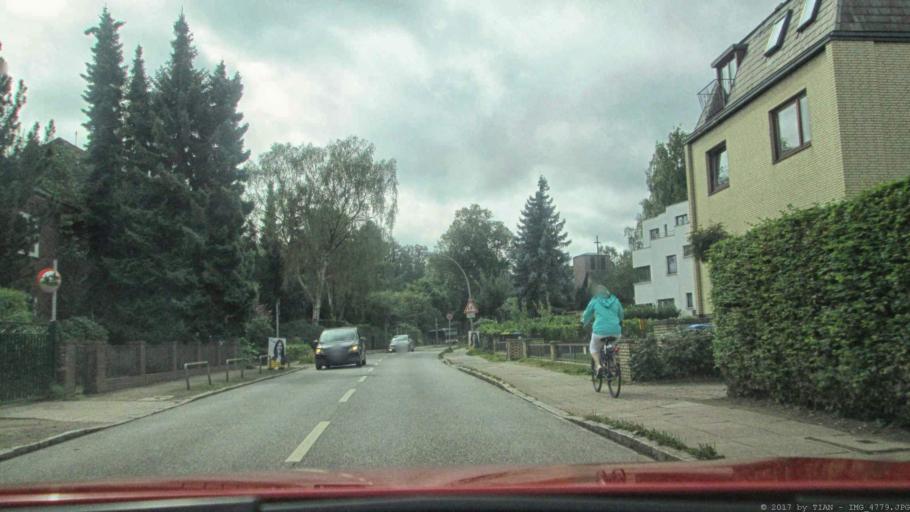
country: DE
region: Schleswig-Holstein
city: Halstenbek
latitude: 53.5623
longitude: 9.8247
